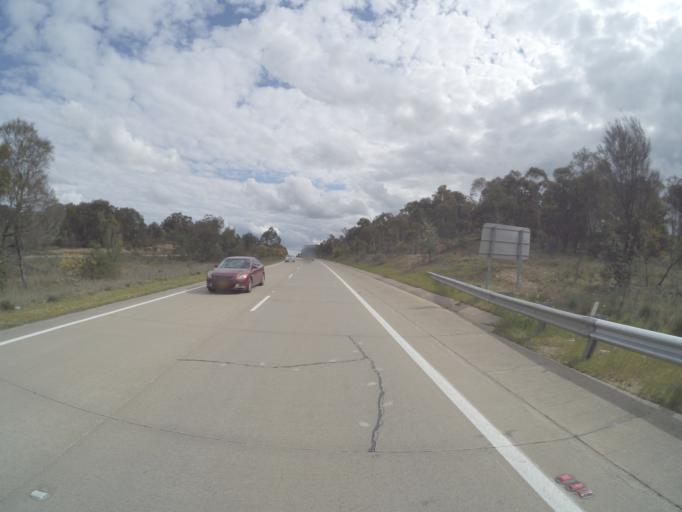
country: AU
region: New South Wales
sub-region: Goulburn Mulwaree
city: Goulburn
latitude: -34.8040
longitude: 149.4935
